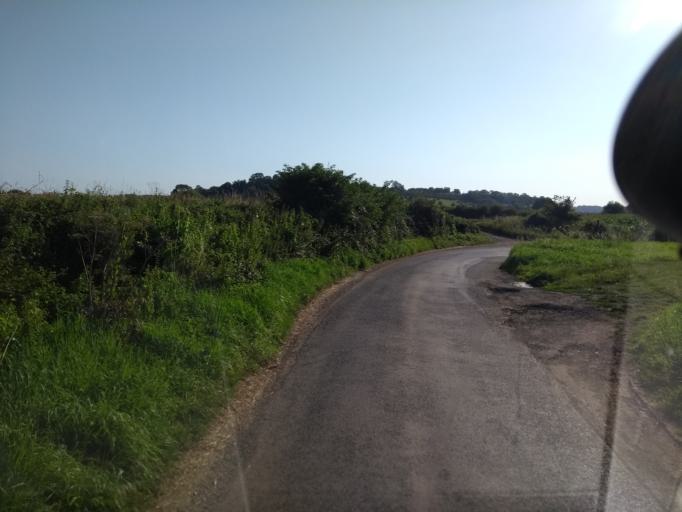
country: GB
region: England
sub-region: Somerset
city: Westonzoyland
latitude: 51.1362
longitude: -2.9360
